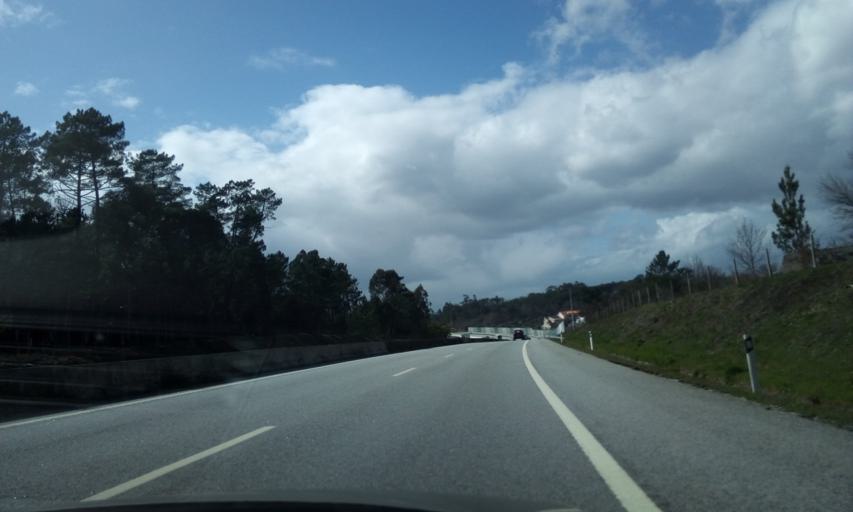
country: PT
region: Viseu
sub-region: Mangualde
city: Mangualde
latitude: 40.6210
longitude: -7.7679
